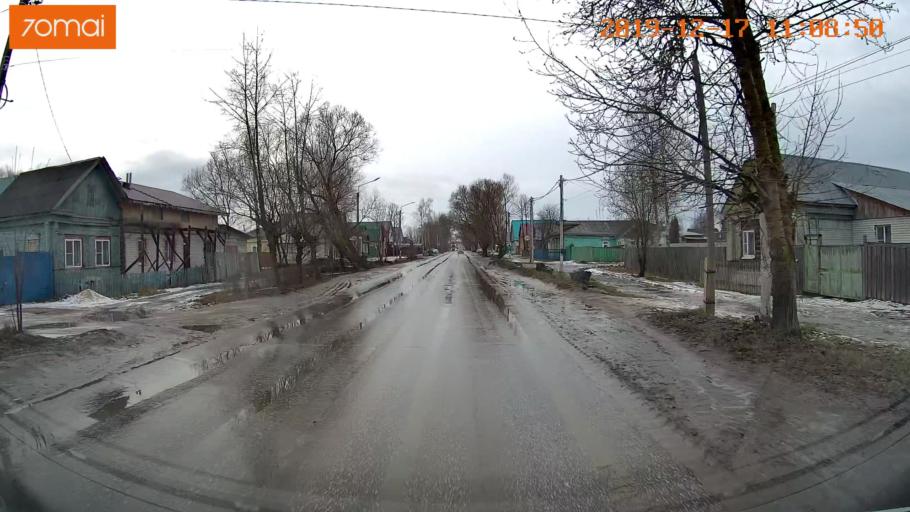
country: RU
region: Vladimir
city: Gus'-Khrustal'nyy
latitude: 55.6053
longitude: 40.6430
